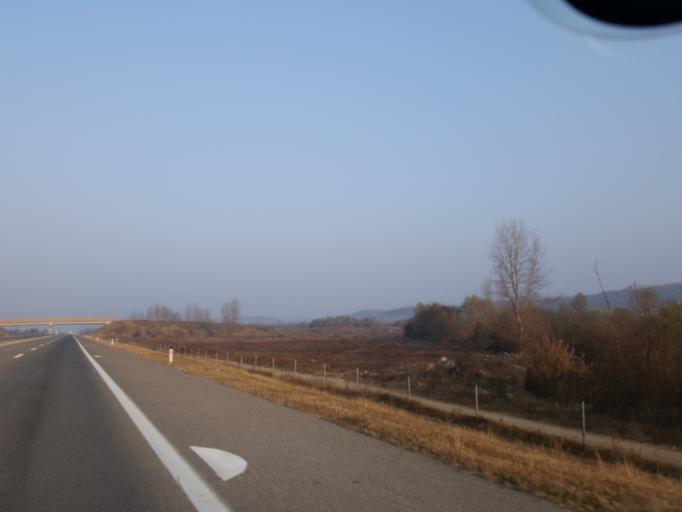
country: RS
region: Central Serbia
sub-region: Jablanicki Okrug
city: Leskovac
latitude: 43.0407
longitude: 21.9931
